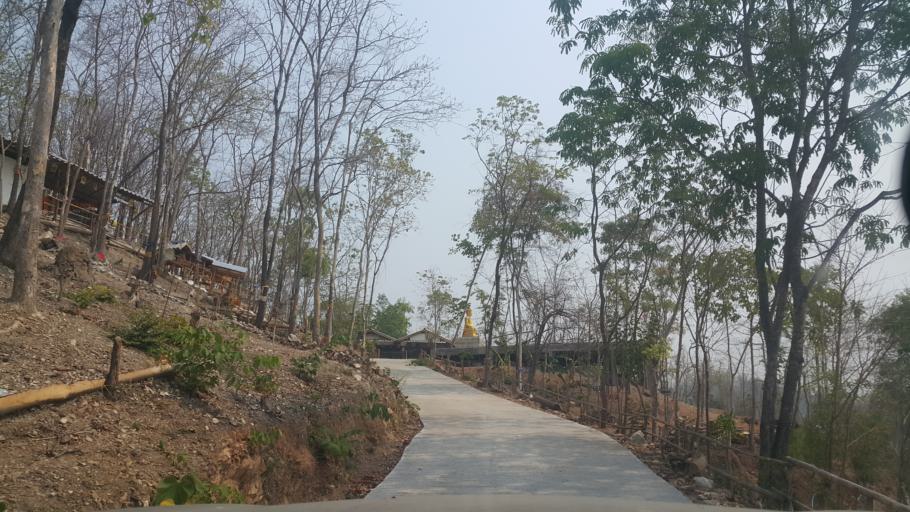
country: TH
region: Lampang
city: Thoen
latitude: 17.7635
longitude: 99.2328
